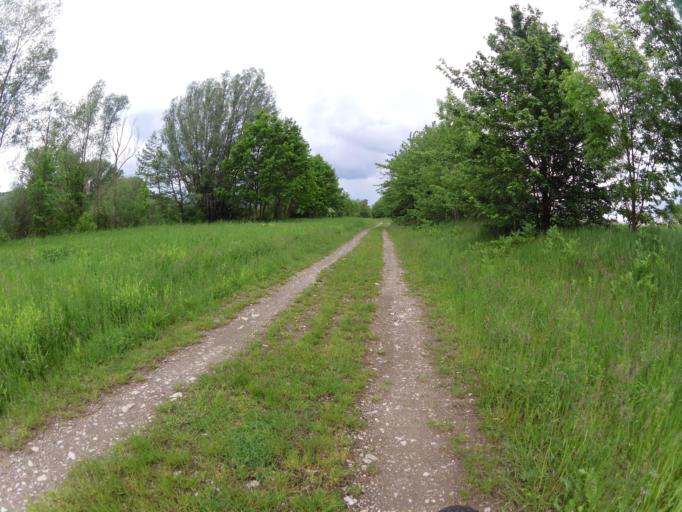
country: DE
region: Bavaria
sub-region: Regierungsbezirk Unterfranken
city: Sommerach
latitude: 49.8222
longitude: 10.2113
